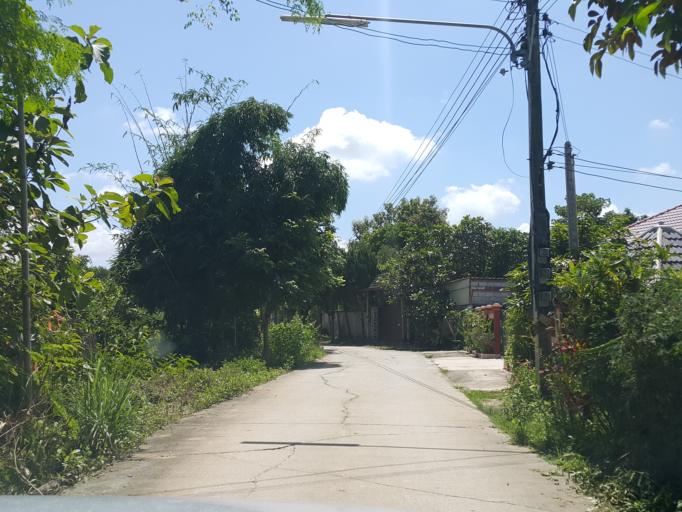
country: TH
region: Chiang Mai
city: San Kamphaeng
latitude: 18.6959
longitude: 99.1135
